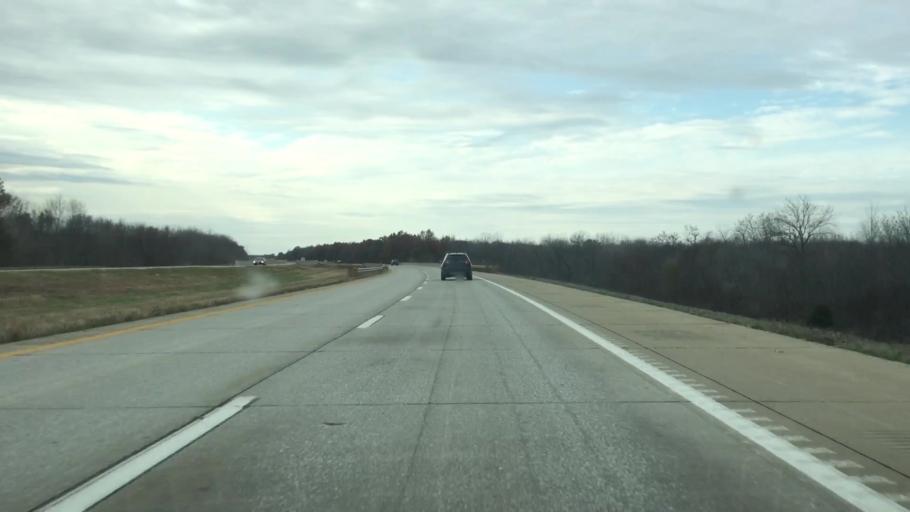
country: US
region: Missouri
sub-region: Henry County
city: Clinton
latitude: 38.4272
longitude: -93.8837
